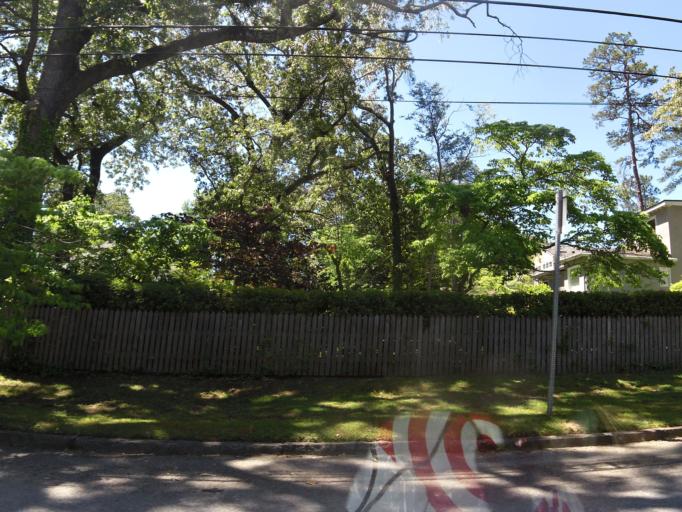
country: US
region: Georgia
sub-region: Richmond County
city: Augusta
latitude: 33.4803
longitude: -82.0263
